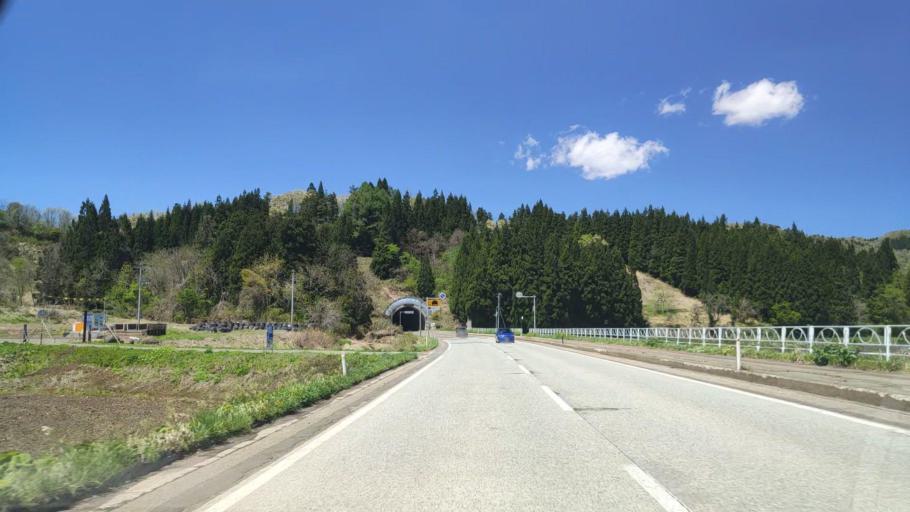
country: JP
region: Akita
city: Yuzawa
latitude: 39.0525
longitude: 140.4424
